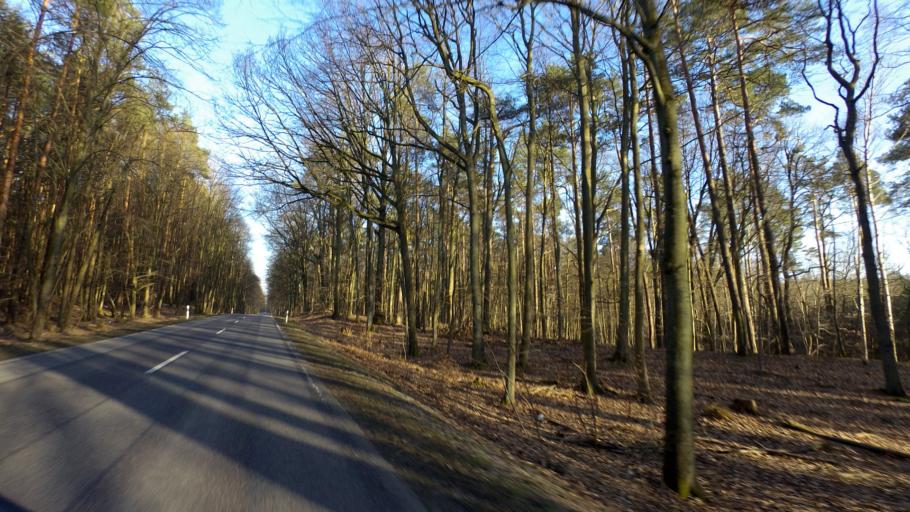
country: DE
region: Brandenburg
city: Joachimsthal
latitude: 52.9551
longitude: 13.7599
